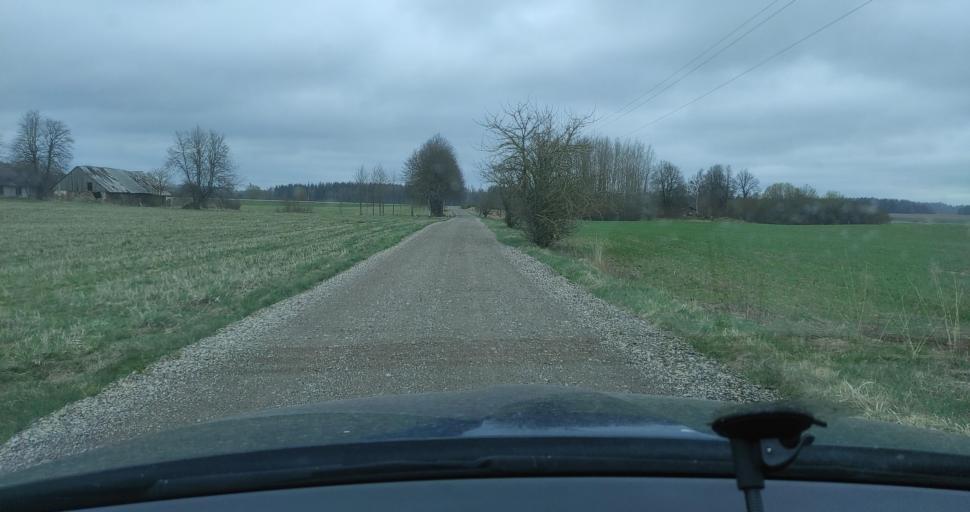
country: LV
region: Saldus Rajons
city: Saldus
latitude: 56.6321
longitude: 22.4260
